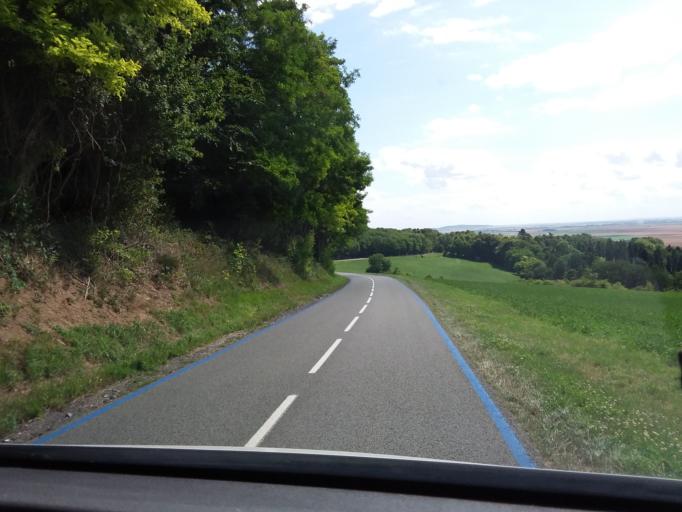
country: FR
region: Picardie
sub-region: Departement de l'Aisne
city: Saint-Erme-Outre-et-Ramecourt
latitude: 49.4450
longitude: 3.7817
